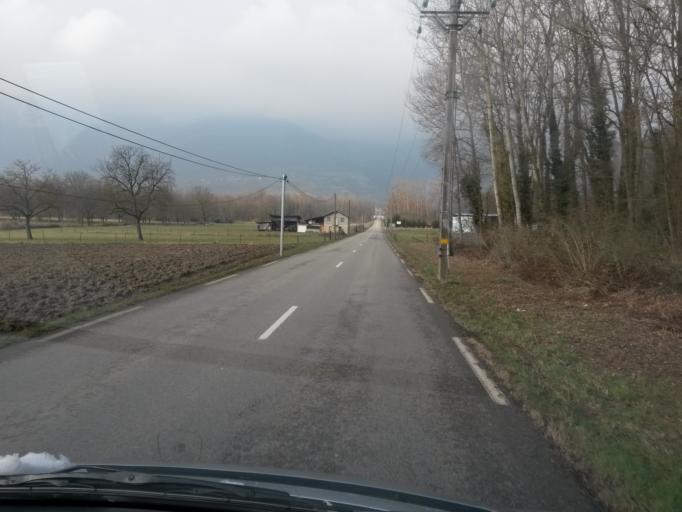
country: FR
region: Rhone-Alpes
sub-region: Departement de l'Isere
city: Tencin
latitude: 45.3119
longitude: 5.9514
